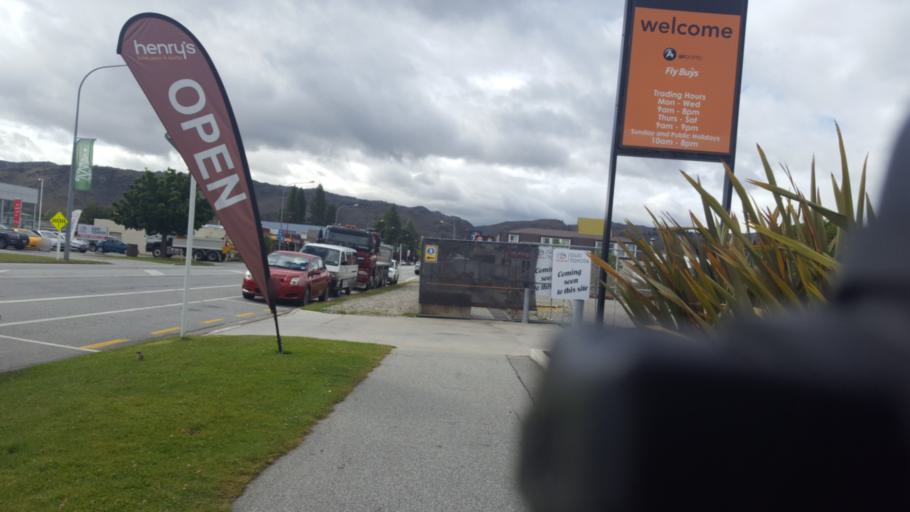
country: NZ
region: Otago
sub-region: Queenstown-Lakes District
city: Wanaka
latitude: -45.2514
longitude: 169.3878
